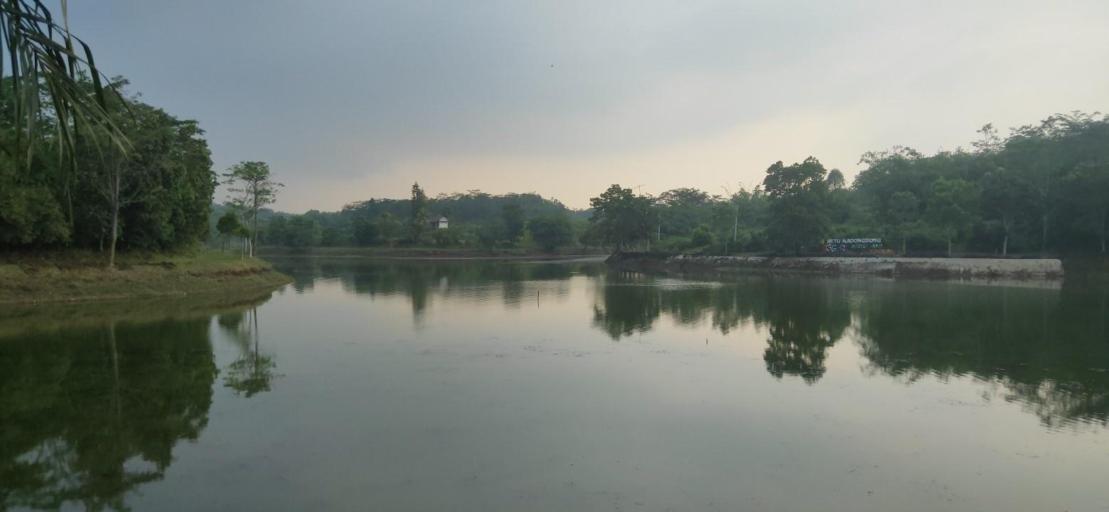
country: ID
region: West Java
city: Pangradin Satu
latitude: -6.4705
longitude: 106.4448
